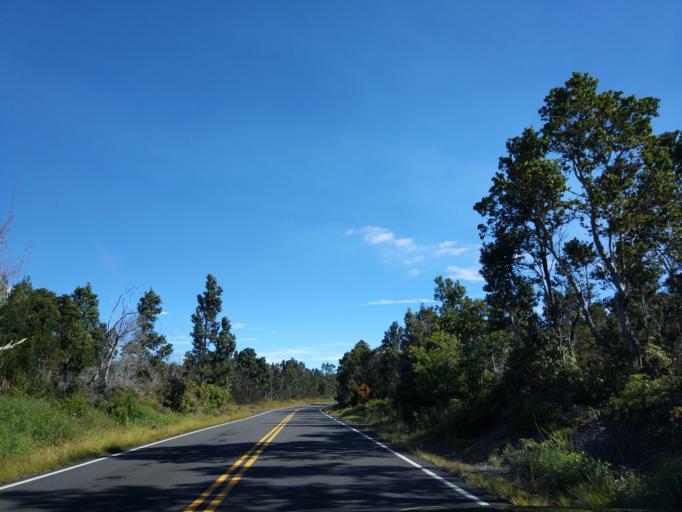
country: US
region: Hawaii
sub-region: Hawaii County
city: Volcano
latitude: 19.3673
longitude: -155.2233
